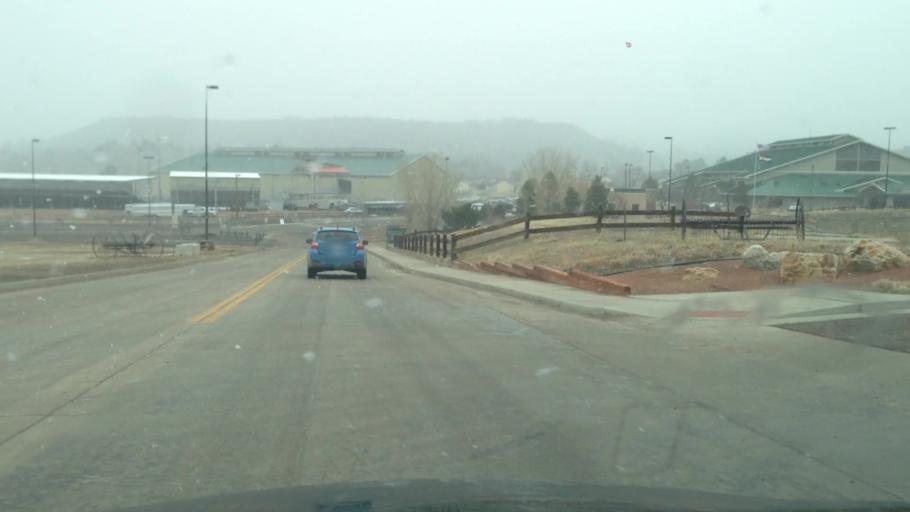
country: US
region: Colorado
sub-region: Douglas County
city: Castle Rock
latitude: 39.3631
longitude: -104.8567
